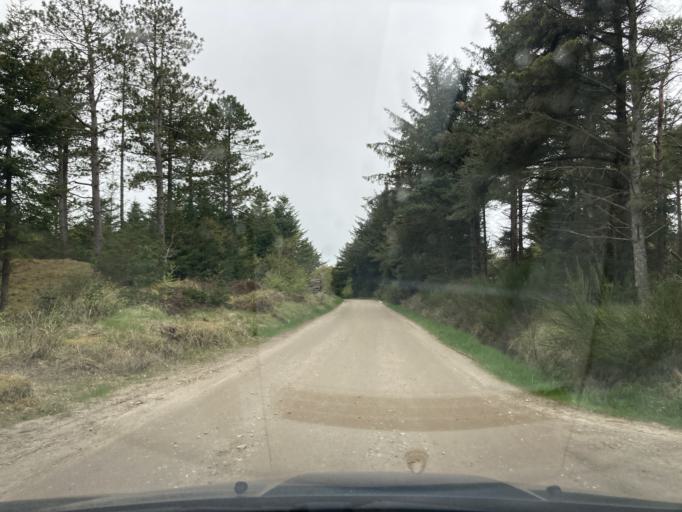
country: DK
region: Central Jutland
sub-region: Lemvig Kommune
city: Thyboron
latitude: 56.8212
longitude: 8.2667
